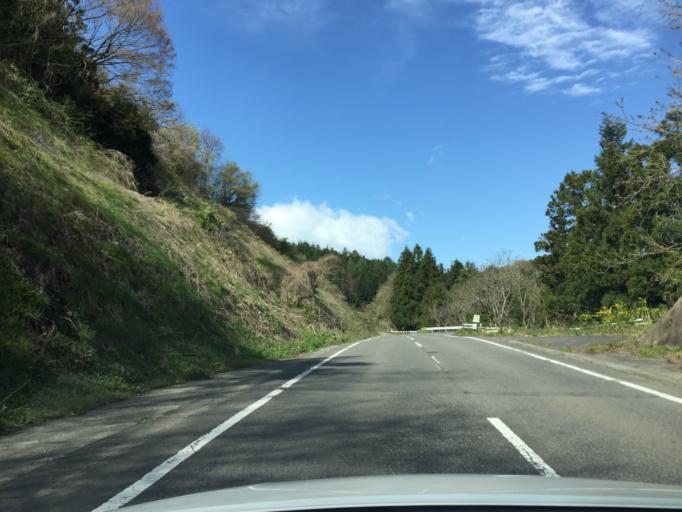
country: JP
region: Fukushima
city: Funehikimachi-funehiki
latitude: 37.5329
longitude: 140.6055
